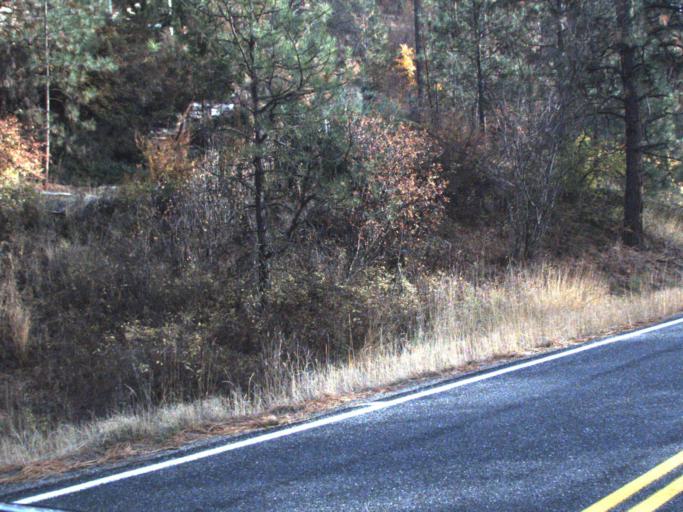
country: US
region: Washington
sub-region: Stevens County
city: Kettle Falls
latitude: 48.3149
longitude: -118.1485
